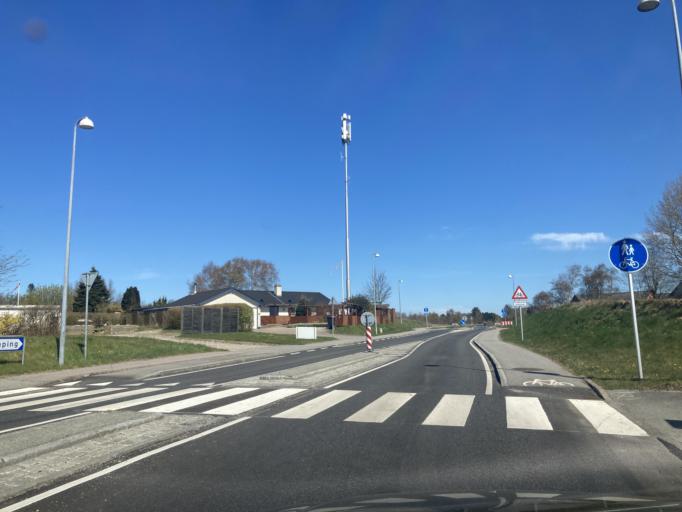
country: DK
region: Capital Region
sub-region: Gribskov Kommune
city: Helsinge
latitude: 56.0888
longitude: 12.2136
